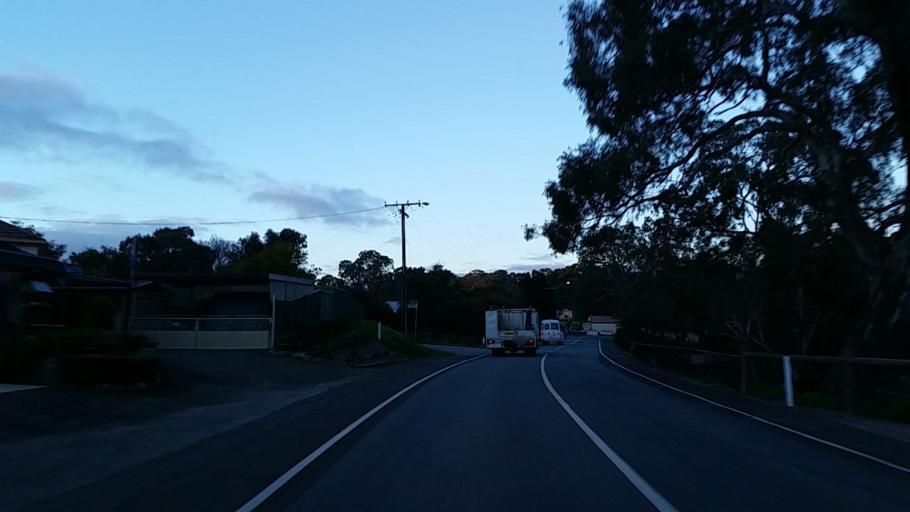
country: AU
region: South Australia
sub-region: Barossa
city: Williamstown
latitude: -34.6737
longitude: 138.8893
